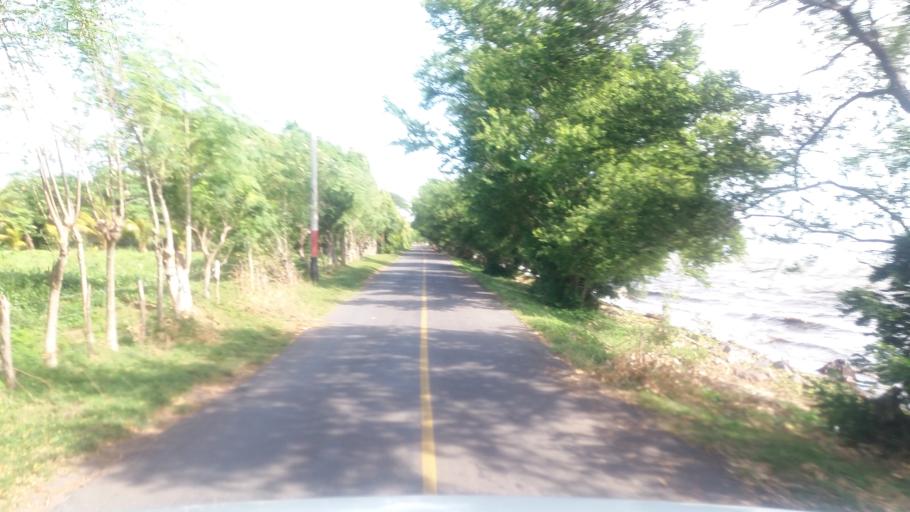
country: NI
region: Granada
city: Granada
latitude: 11.9788
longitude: -85.9414
